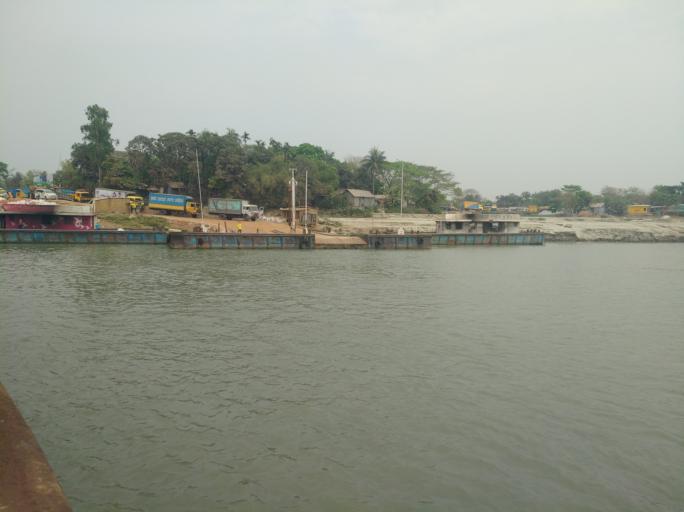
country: BD
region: Dhaka
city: Faridpur
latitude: 23.7854
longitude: 89.8115
